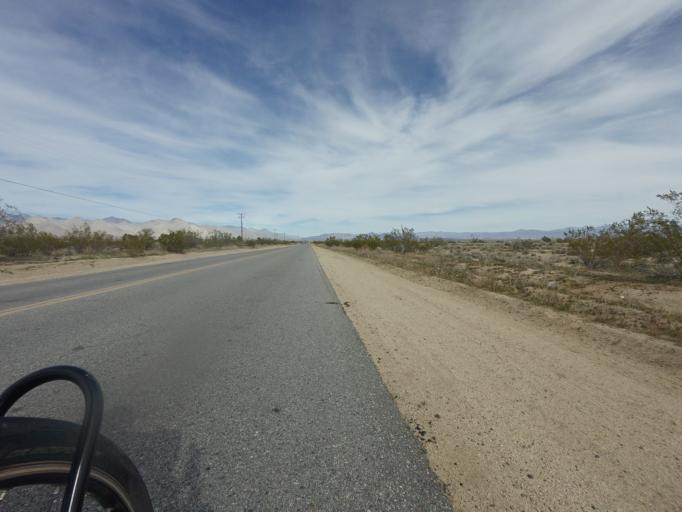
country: US
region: California
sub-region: Kern County
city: Inyokern
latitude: 35.6895
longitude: -117.8249
